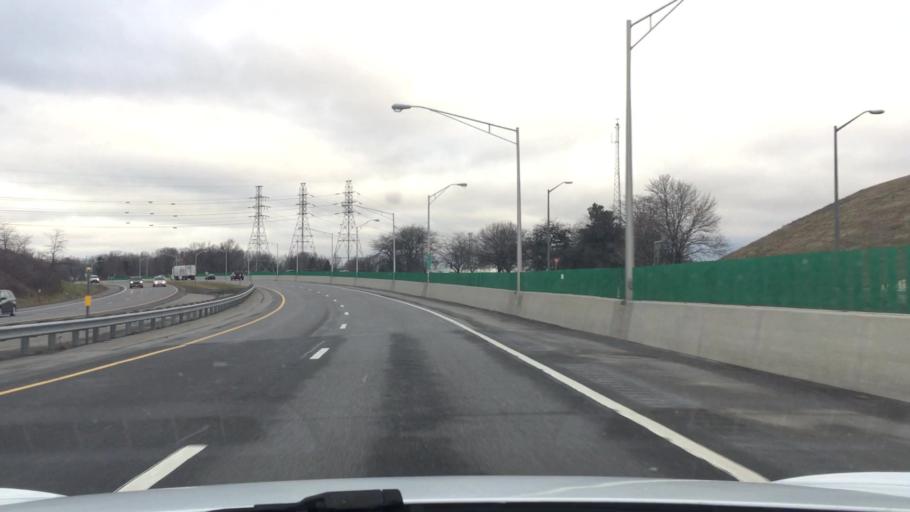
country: US
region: New York
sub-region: Niagara County
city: Lewiston
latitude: 43.1444
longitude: -79.0222
